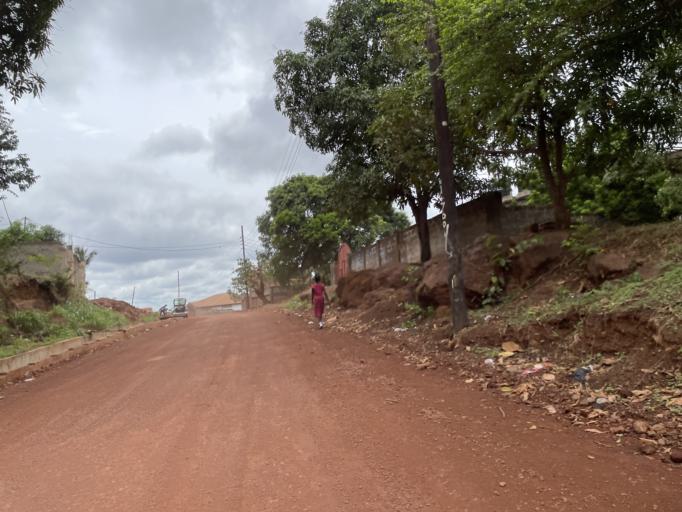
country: SL
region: Western Area
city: Hastings
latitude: 8.4005
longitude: -13.1451
